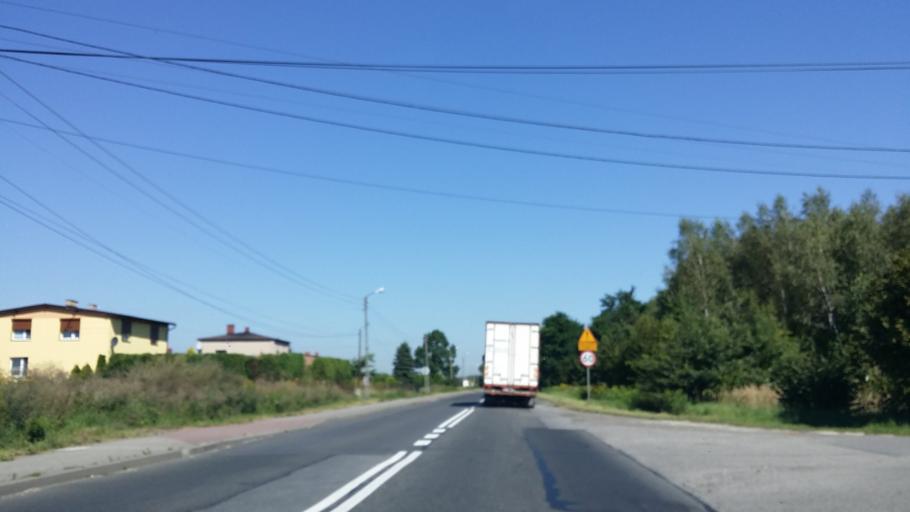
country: PL
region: Silesian Voivodeship
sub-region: Powiat bierunsko-ledzinski
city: Chelm Slaski
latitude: 50.1207
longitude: 19.2003
